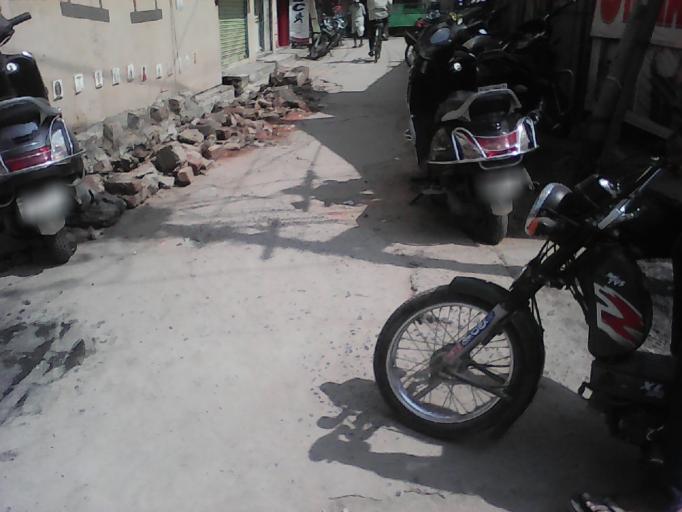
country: IN
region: Andhra Pradesh
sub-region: Guntur
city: Bhattiprolu
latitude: 16.2370
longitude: 80.6496
